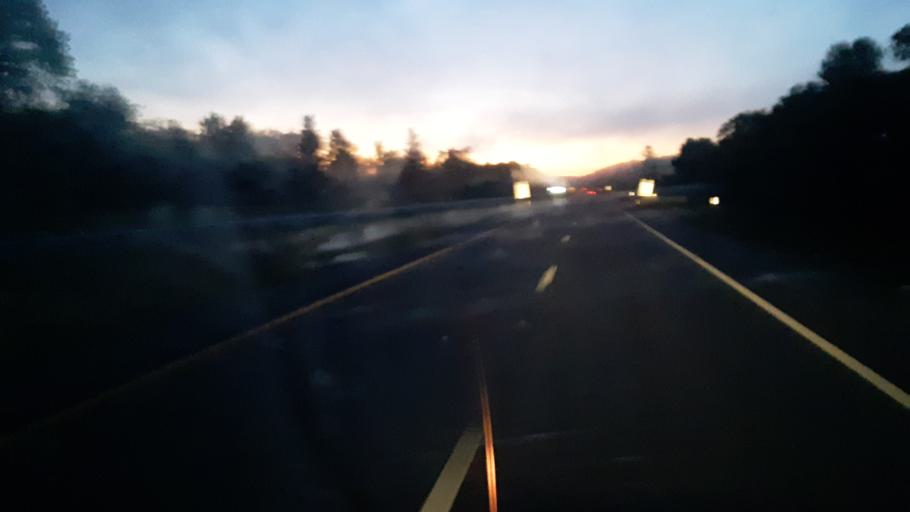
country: US
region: New York
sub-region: Montgomery County
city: Fonda
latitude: 42.9227
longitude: -74.4308
